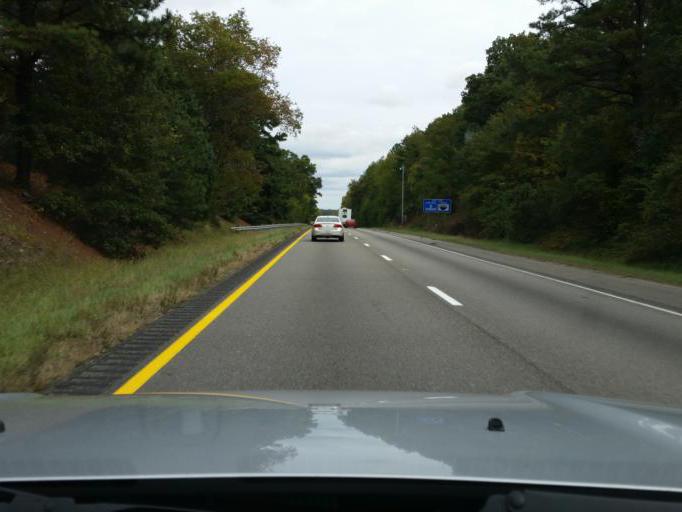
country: US
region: Virginia
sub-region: Henrico County
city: Sandston
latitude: 37.5155
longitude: -77.2252
